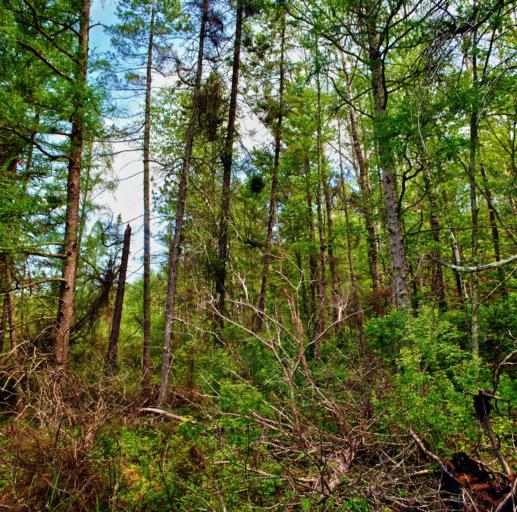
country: US
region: Wisconsin
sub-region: Sawyer County
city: Hayward
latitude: 46.0155
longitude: -91.5325
